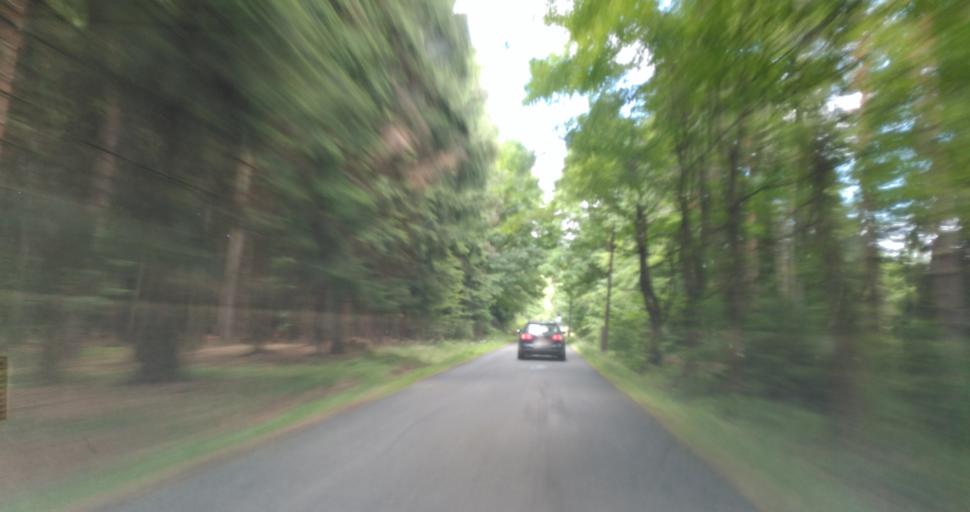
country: CZ
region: Plzensky
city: Zbiroh
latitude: 49.8953
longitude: 13.8084
